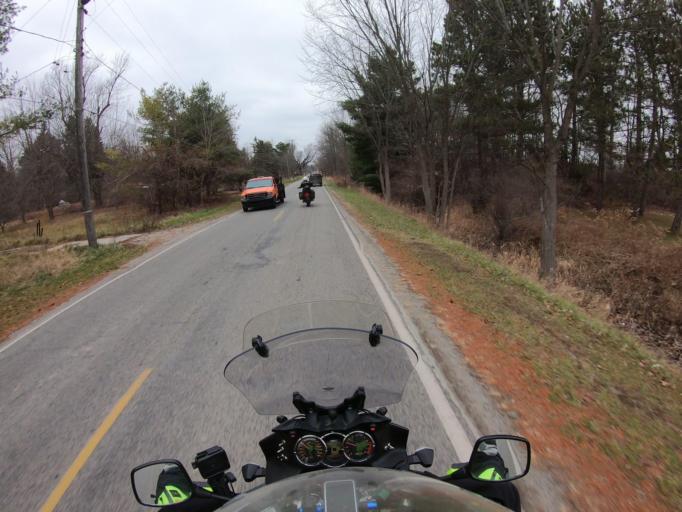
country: US
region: Michigan
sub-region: Saginaw County
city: Saint Charles
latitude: 43.2865
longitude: -84.1360
